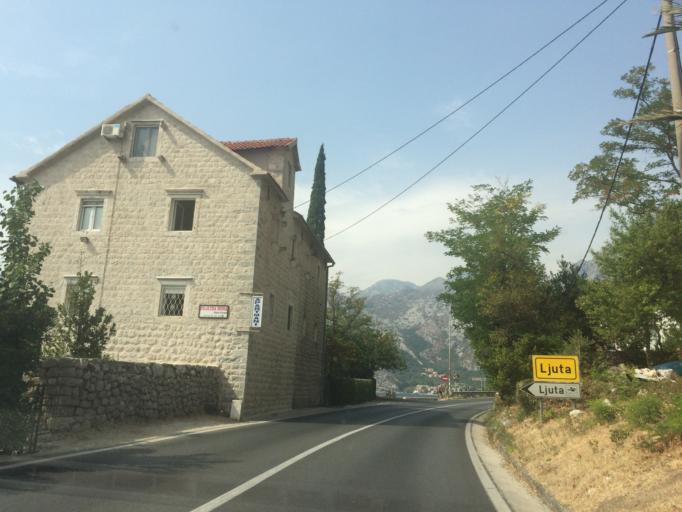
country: ME
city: Dobrota
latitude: 42.4769
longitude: 18.7638
